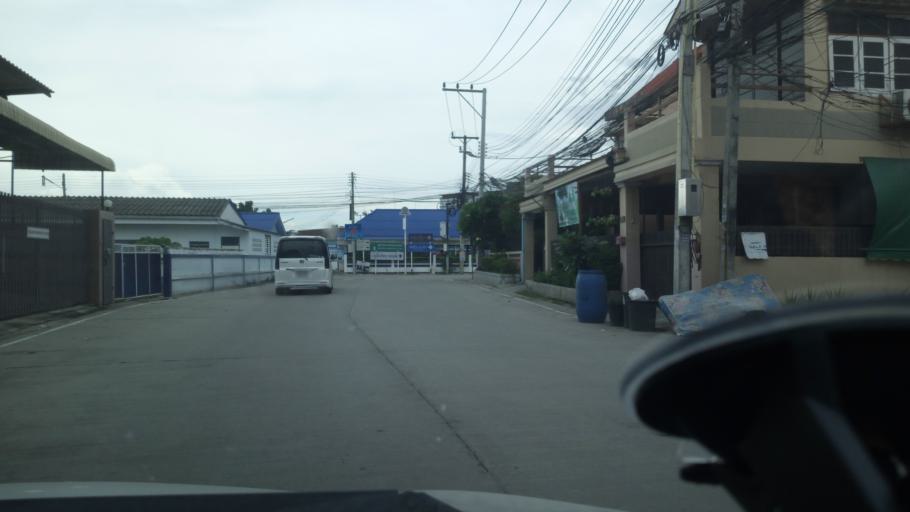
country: TH
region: Chon Buri
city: Chon Buri
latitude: 13.2883
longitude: 100.9290
